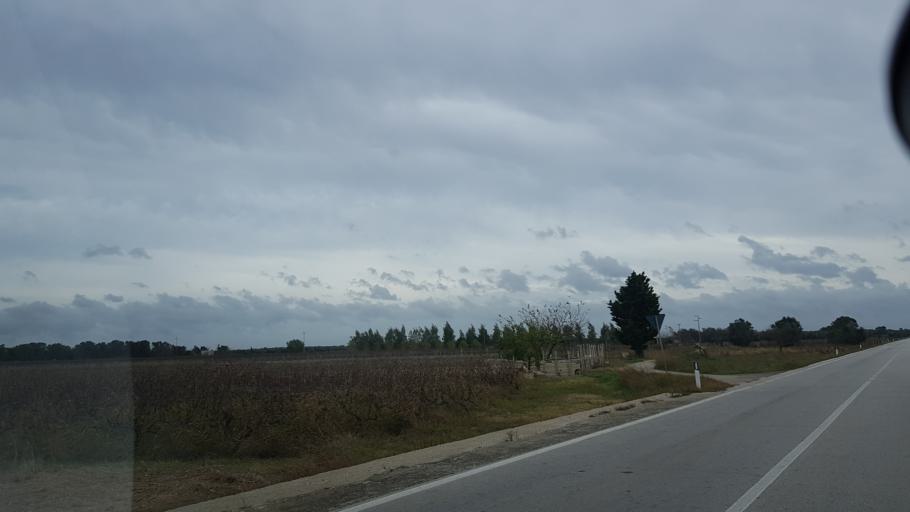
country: IT
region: Apulia
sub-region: Provincia di Lecce
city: Guagnano
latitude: 40.4023
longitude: 17.9063
